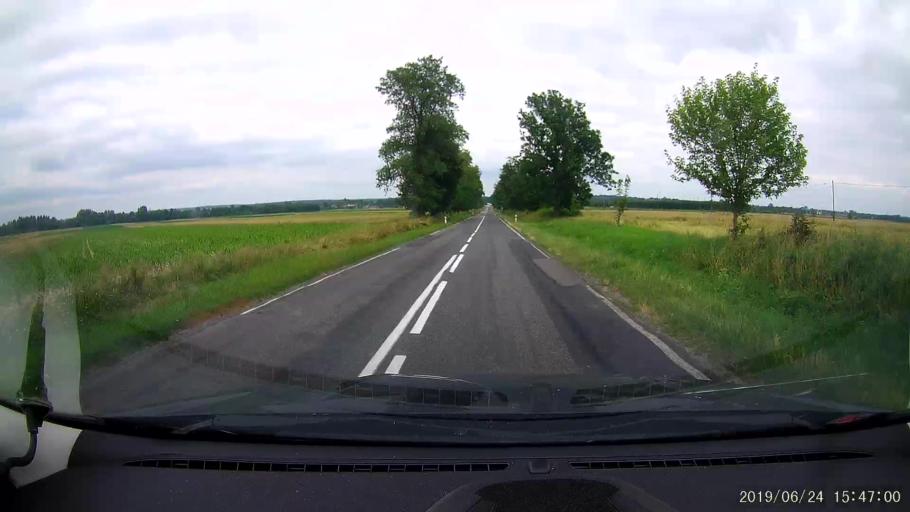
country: PL
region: Subcarpathian Voivodeship
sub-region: Powiat lubaczowski
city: Oleszyce
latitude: 50.1597
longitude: 23.0113
